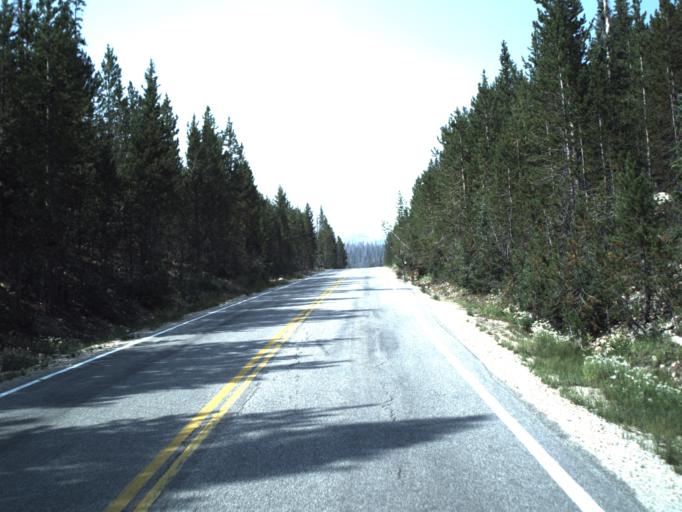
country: US
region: Utah
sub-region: Summit County
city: Kamas
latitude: 40.6612
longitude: -110.9464
